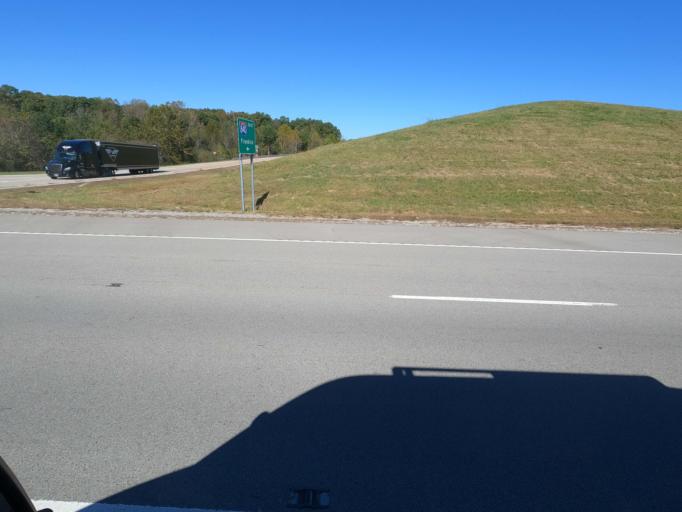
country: US
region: Tennessee
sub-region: Williamson County
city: Fairview
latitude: 35.9392
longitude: -87.1912
